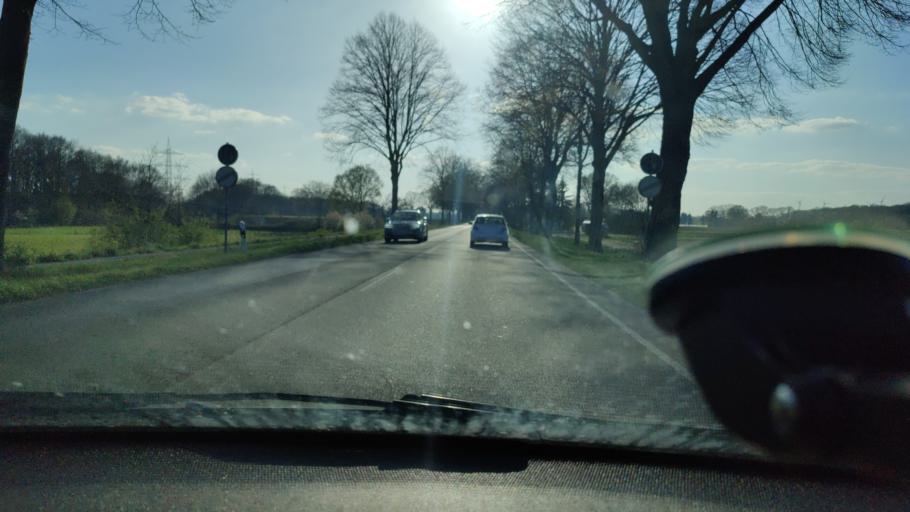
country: DE
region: North Rhine-Westphalia
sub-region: Regierungsbezirk Dusseldorf
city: Schermbeck
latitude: 51.6811
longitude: 6.8383
